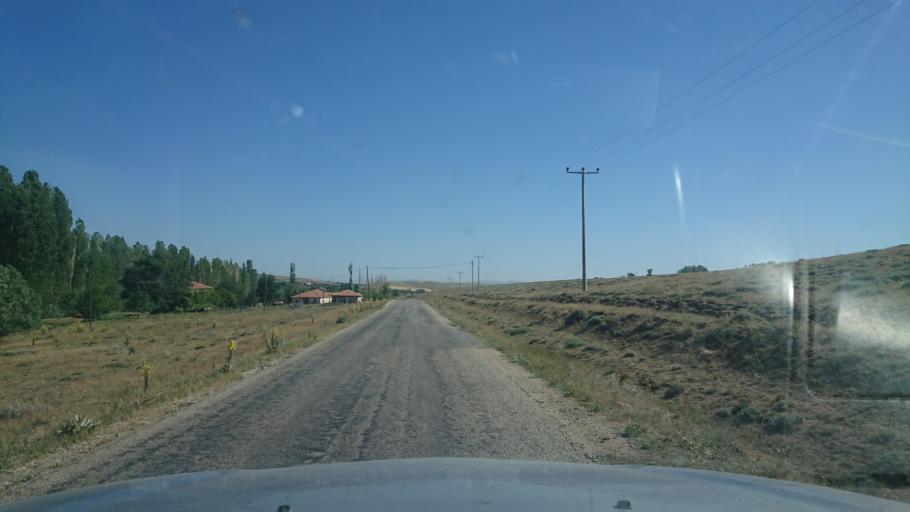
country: TR
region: Aksaray
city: Agacoren
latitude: 38.8729
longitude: 33.8802
